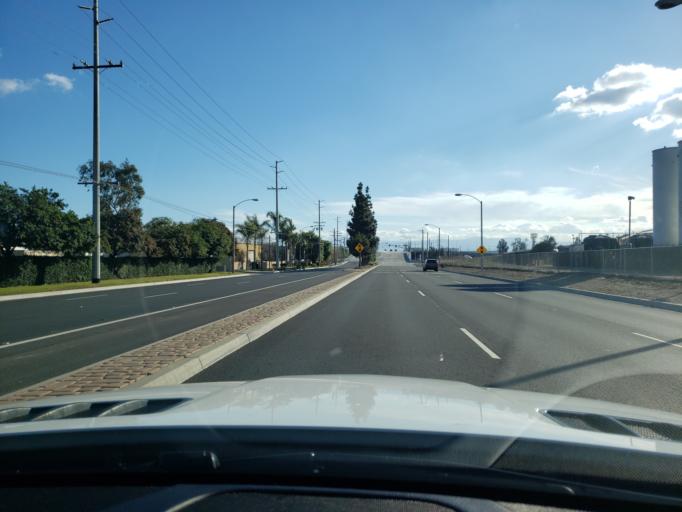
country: US
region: California
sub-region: Riverside County
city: Mira Loma
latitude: 34.0369
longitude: -117.5584
